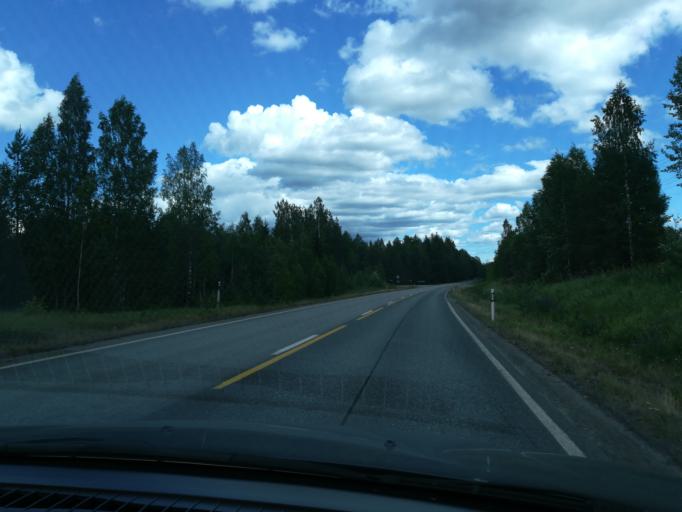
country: FI
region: Southern Savonia
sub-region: Mikkeli
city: Hirvensalmi
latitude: 61.6714
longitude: 26.8334
